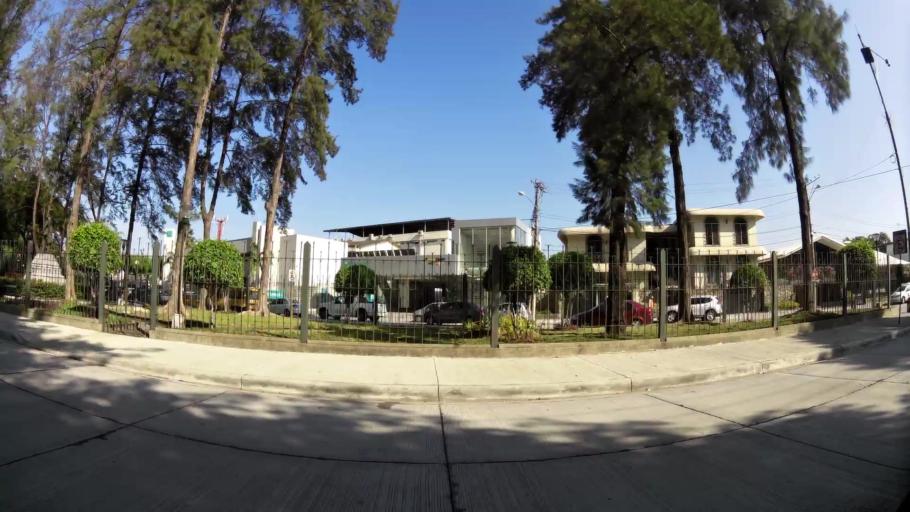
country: EC
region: Guayas
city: Guayaquil
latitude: -2.1751
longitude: -79.9043
